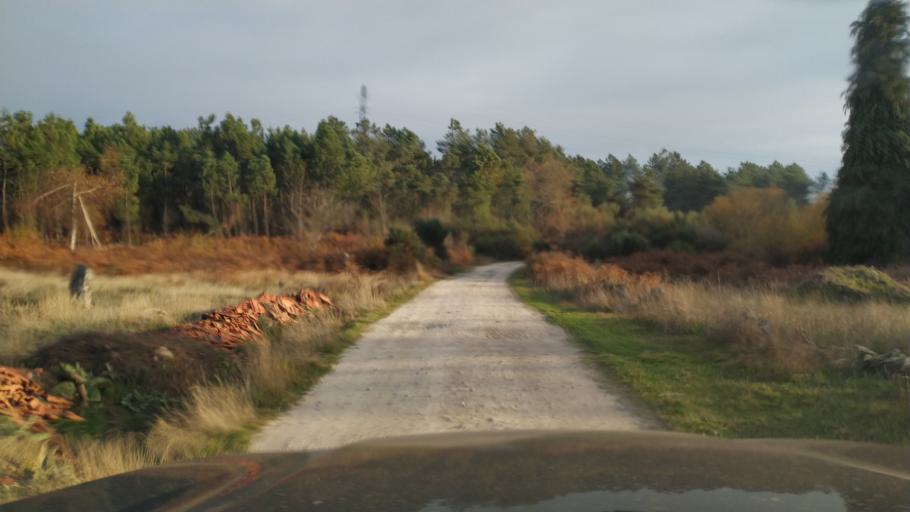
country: PT
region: Vila Real
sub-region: Sabrosa
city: Sabrosa
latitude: 41.3245
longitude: -7.6236
